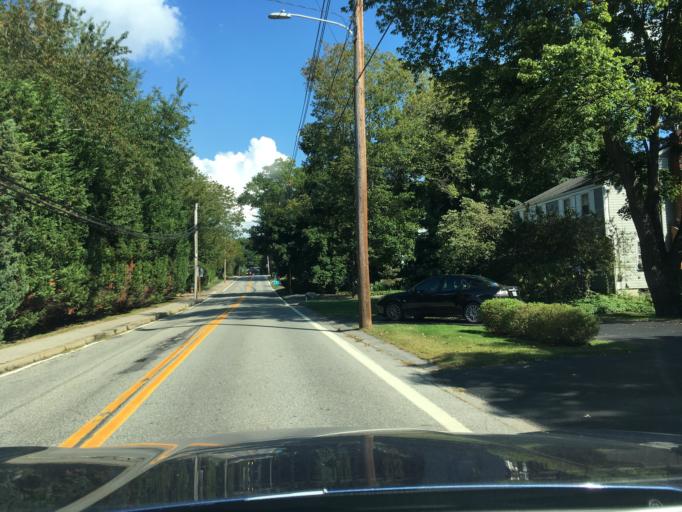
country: US
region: Rhode Island
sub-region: Bristol County
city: Barrington
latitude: 41.7292
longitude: -71.3048
